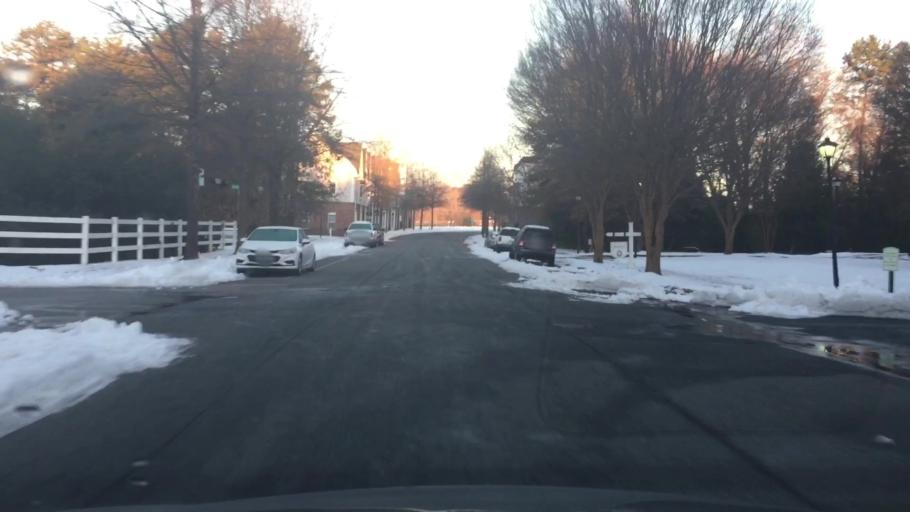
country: US
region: North Carolina
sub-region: Mecklenburg County
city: Cornelius
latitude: 35.4992
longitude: -80.8627
